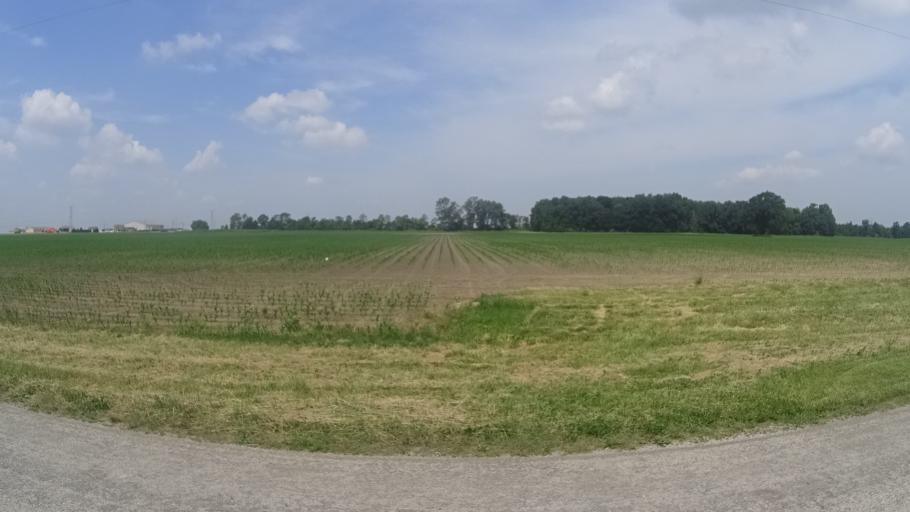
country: US
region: Ohio
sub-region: Erie County
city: Sandusky
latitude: 41.3535
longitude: -82.6943
